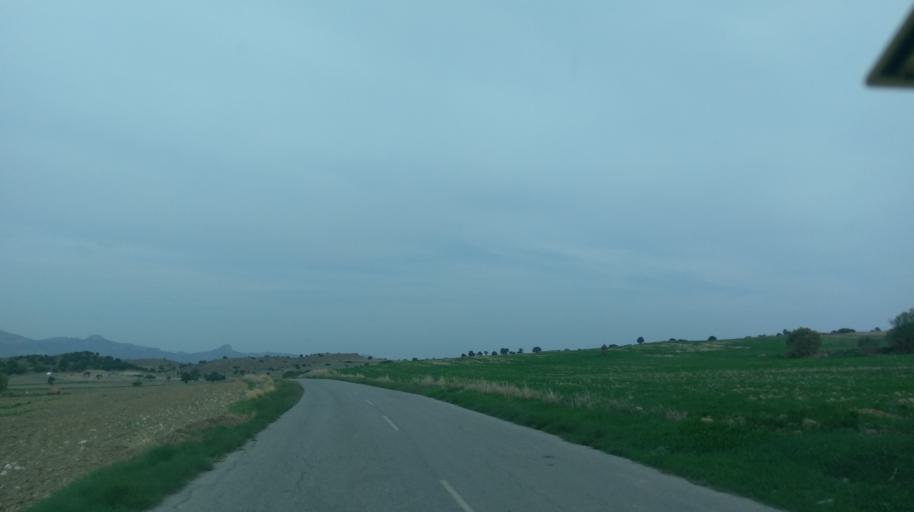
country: CY
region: Ammochostos
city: Trikomo
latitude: 35.3357
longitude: 33.9293
